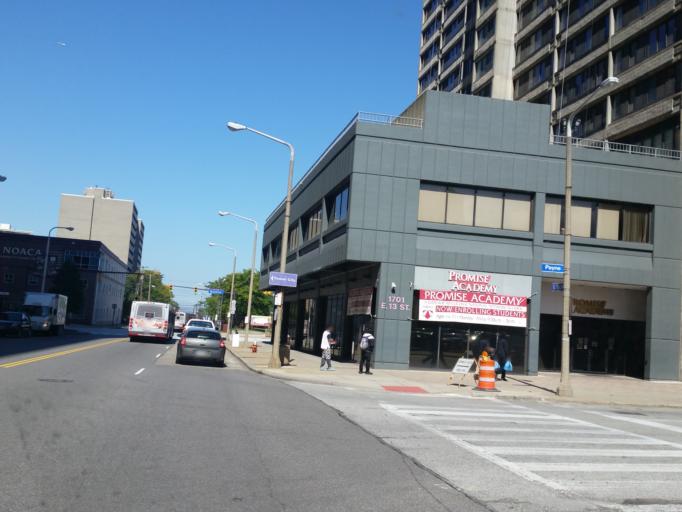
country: US
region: Ohio
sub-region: Cuyahoga County
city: Cleveland
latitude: 41.5036
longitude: -81.6842
